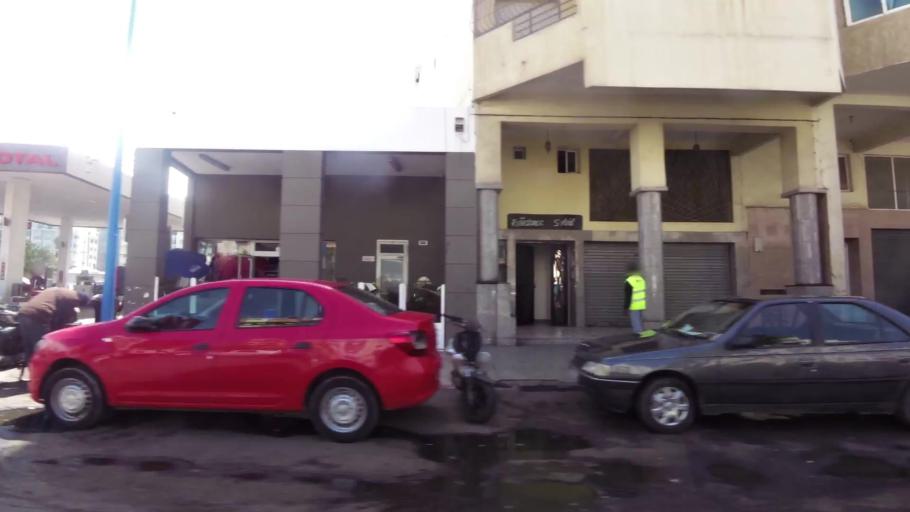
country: MA
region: Grand Casablanca
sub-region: Casablanca
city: Casablanca
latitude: 33.5995
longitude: -7.6354
